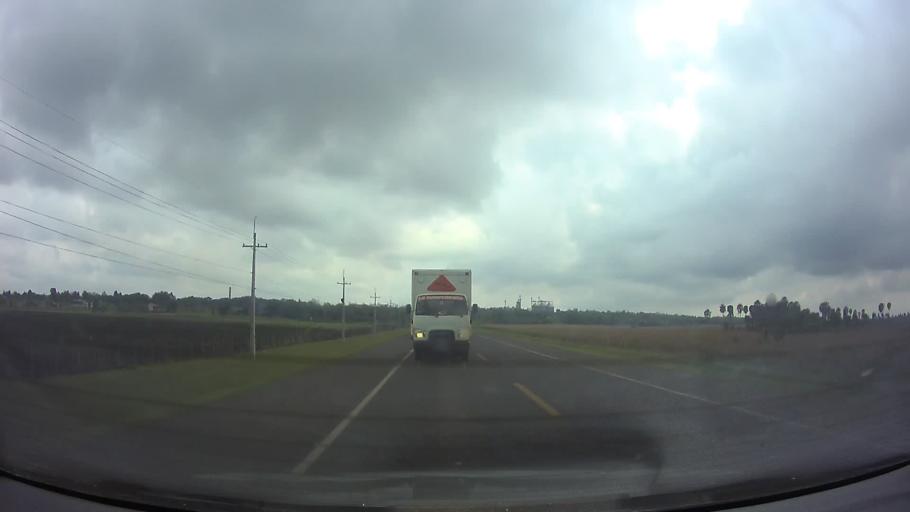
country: PY
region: Cordillera
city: Arroyos y Esteros
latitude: -25.0650
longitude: -57.1986
